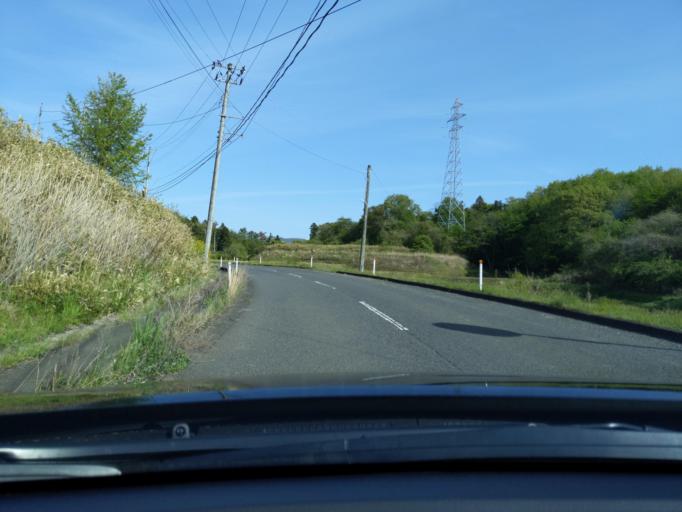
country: JP
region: Fukushima
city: Sukagawa
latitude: 37.3047
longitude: 140.4220
